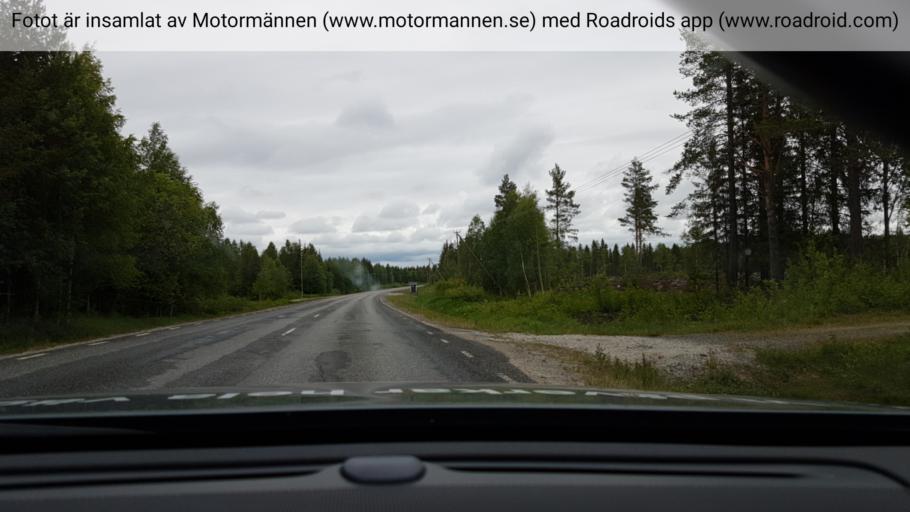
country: SE
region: Vaesterbotten
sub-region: Lycksele Kommun
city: Lycksele
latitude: 64.5501
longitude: 18.5088
